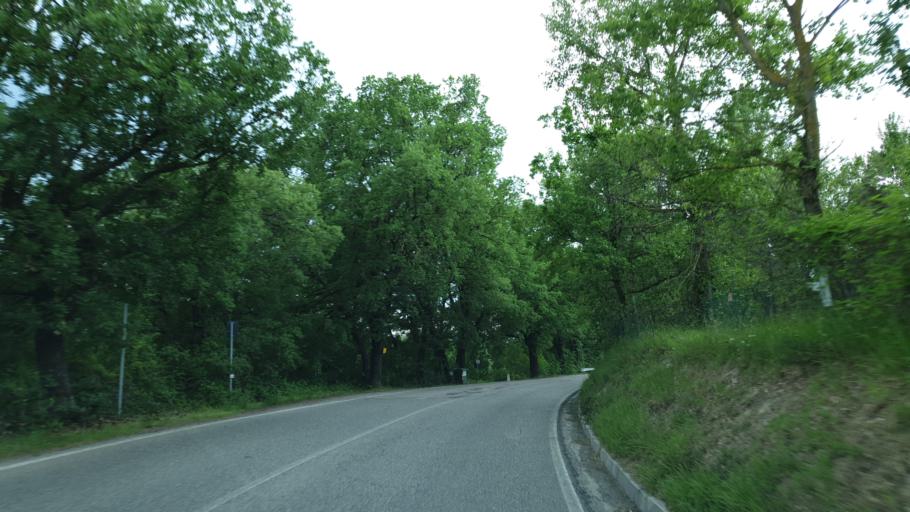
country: IT
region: Emilia-Romagna
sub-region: Provincia di Rimini
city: Secchiano
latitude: 43.9110
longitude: 12.3040
